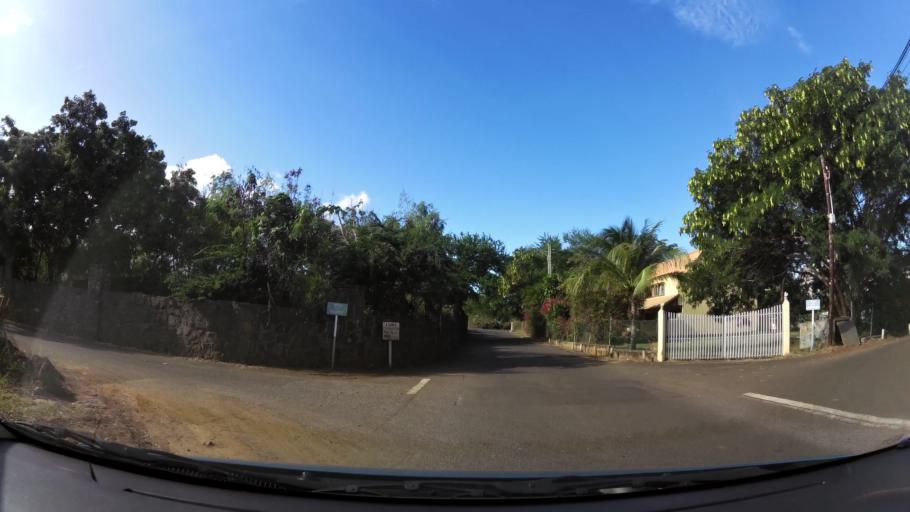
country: MU
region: Black River
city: Albion
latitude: -20.2050
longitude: 57.4091
